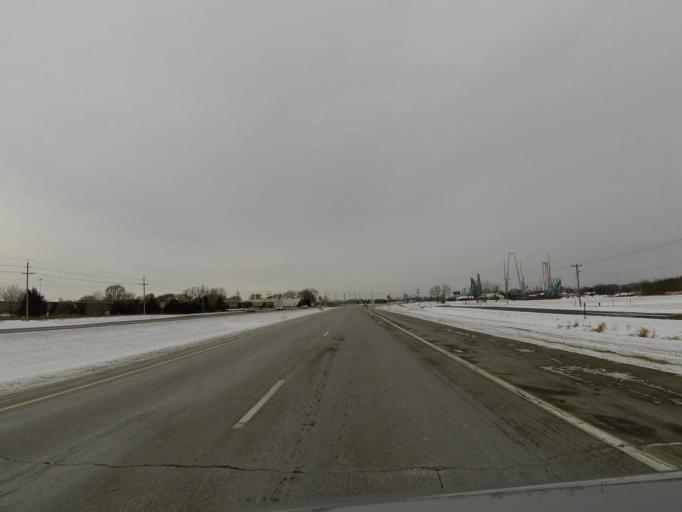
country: US
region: Minnesota
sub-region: Hennepin County
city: Eden Prairie
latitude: 44.7956
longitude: -93.4432
